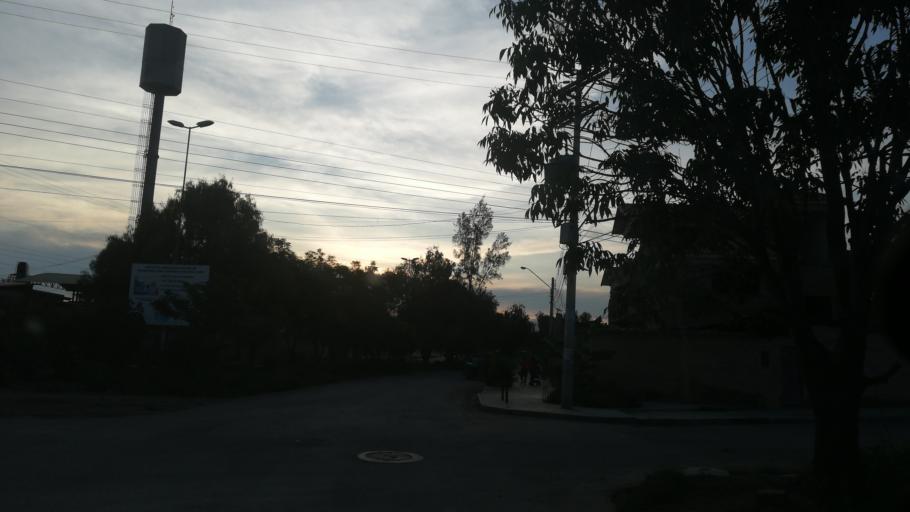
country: BO
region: Cochabamba
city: Cochabamba
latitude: -17.3830
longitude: -66.2068
